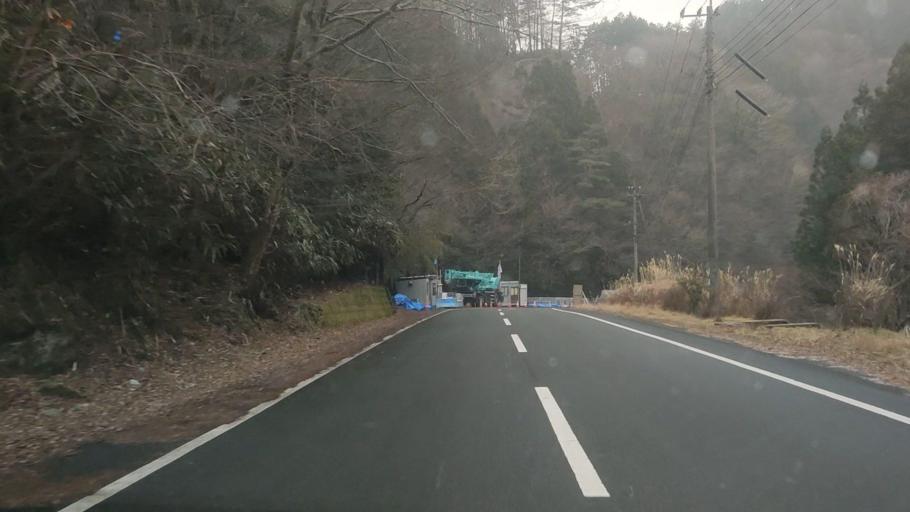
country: JP
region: Kumamoto
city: Matsubase
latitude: 32.5539
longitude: 130.9333
